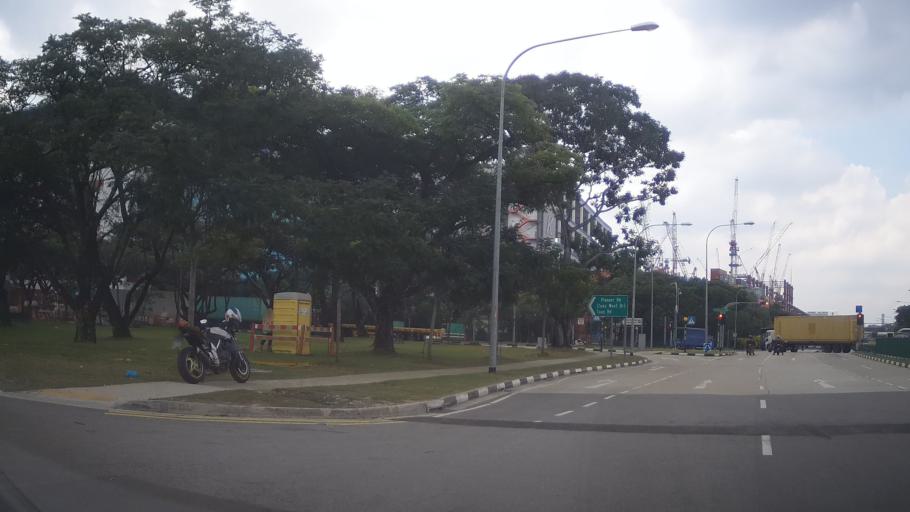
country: SG
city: Singapore
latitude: 1.3089
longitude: 103.6785
